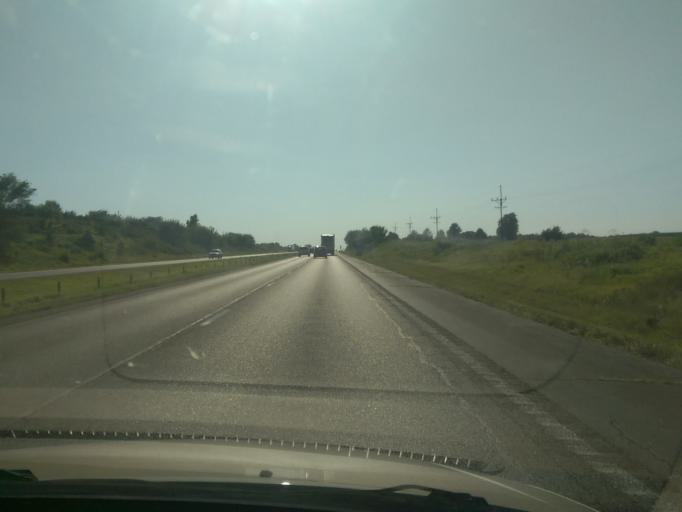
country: US
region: Missouri
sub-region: Lafayette County
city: Higginsville
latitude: 39.0022
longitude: -93.7909
